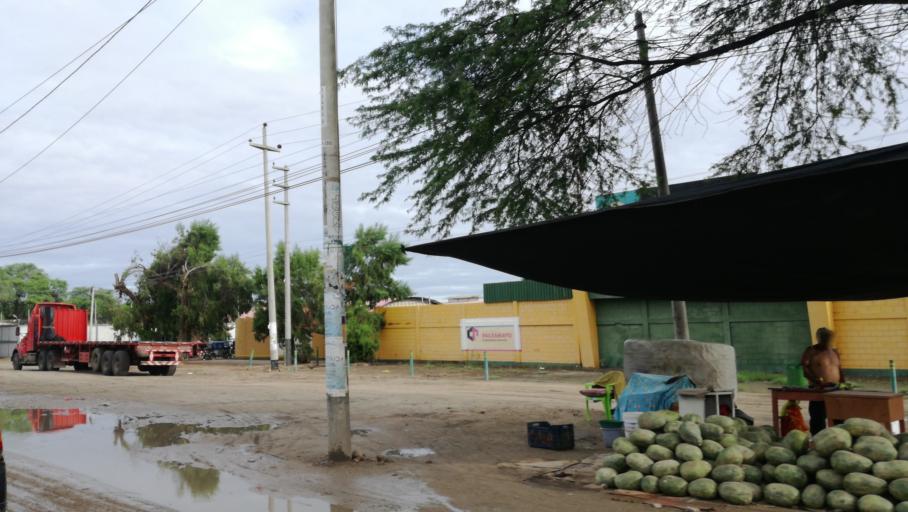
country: PE
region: Piura
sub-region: Provincia de Piura
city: Piura
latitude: -5.1823
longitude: -80.6560
